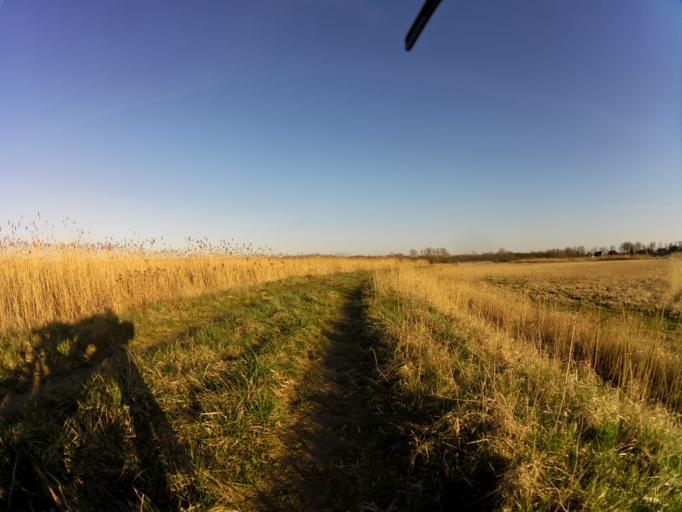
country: PL
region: West Pomeranian Voivodeship
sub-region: Powiat policki
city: Nowe Warpno
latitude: 53.7267
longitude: 14.2968
